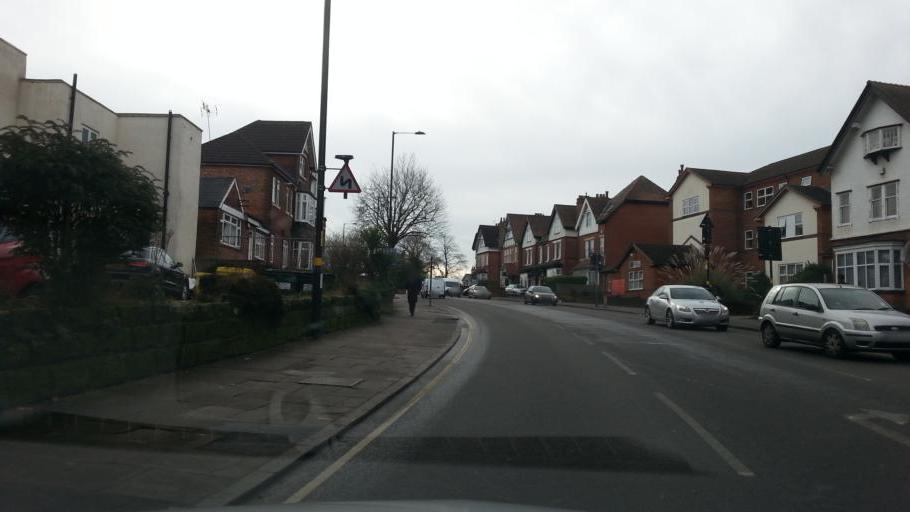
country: GB
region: England
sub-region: City and Borough of Birmingham
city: Birmingham
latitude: 52.4439
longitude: -1.8917
